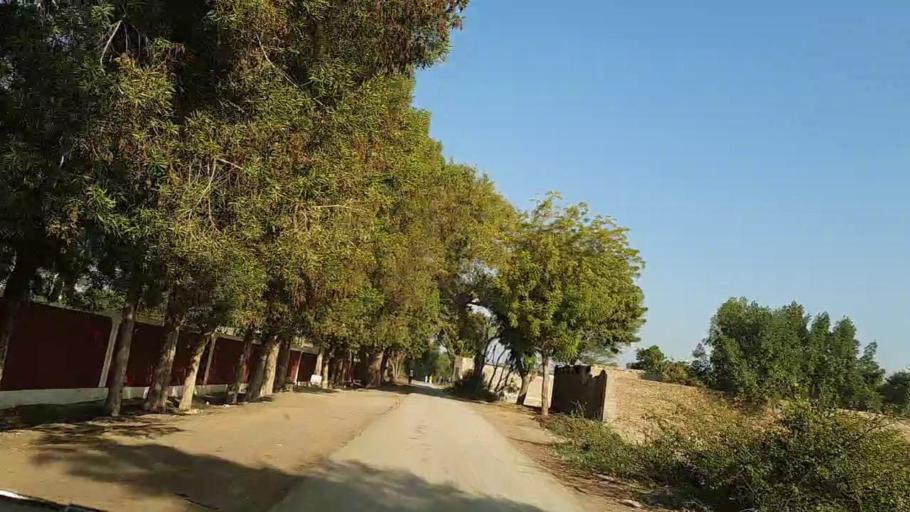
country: PK
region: Sindh
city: Sakrand
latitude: 26.1296
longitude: 68.2192
